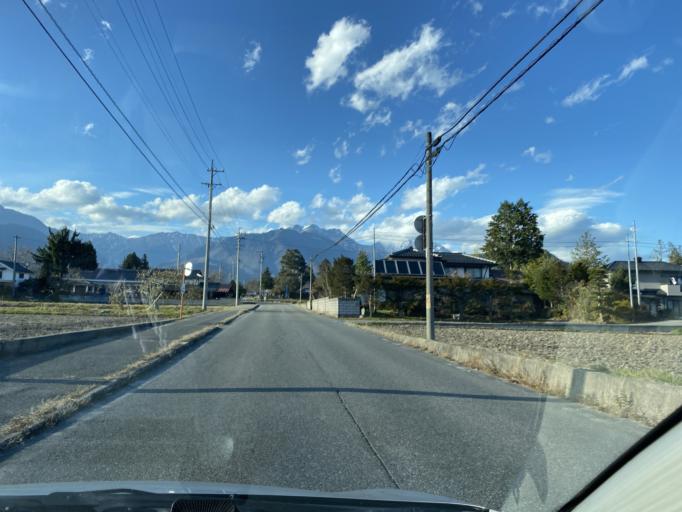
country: JP
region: Nagano
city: Omachi
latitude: 36.5188
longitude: 137.8402
